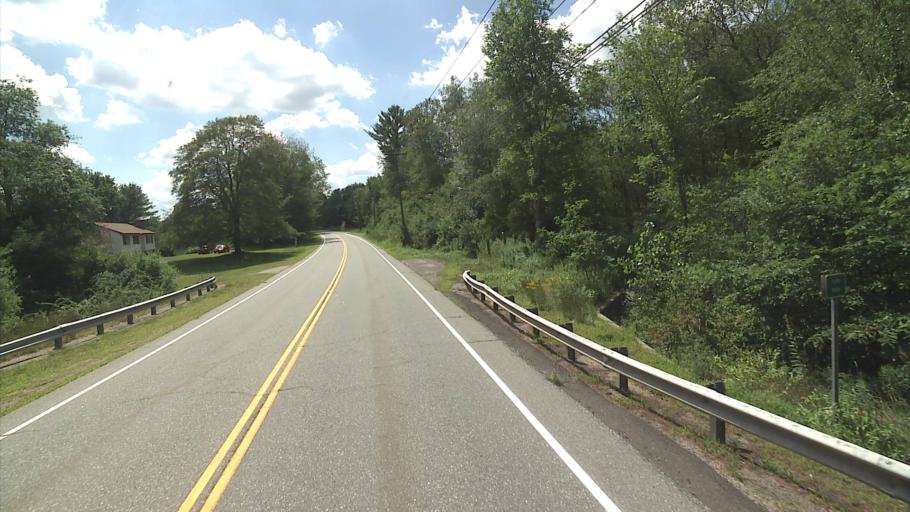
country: US
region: Connecticut
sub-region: Tolland County
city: Storrs
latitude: 41.8502
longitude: -72.0966
